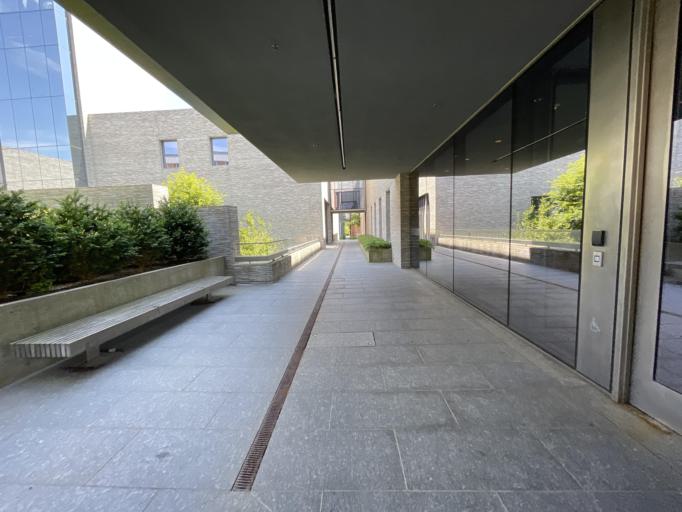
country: US
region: New Jersey
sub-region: Mercer County
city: Princeton
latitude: 40.3498
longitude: -74.6508
